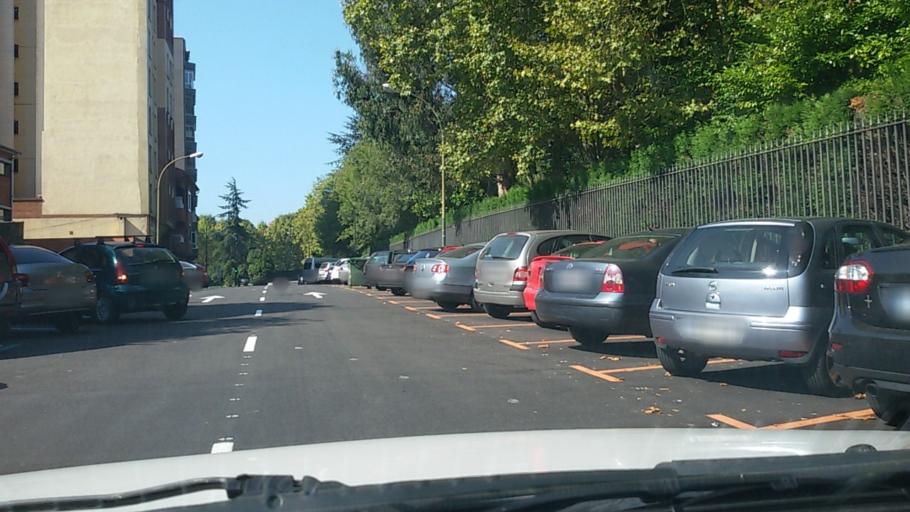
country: ES
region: Asturias
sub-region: Province of Asturias
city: Aviles
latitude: 43.5521
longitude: -5.9213
